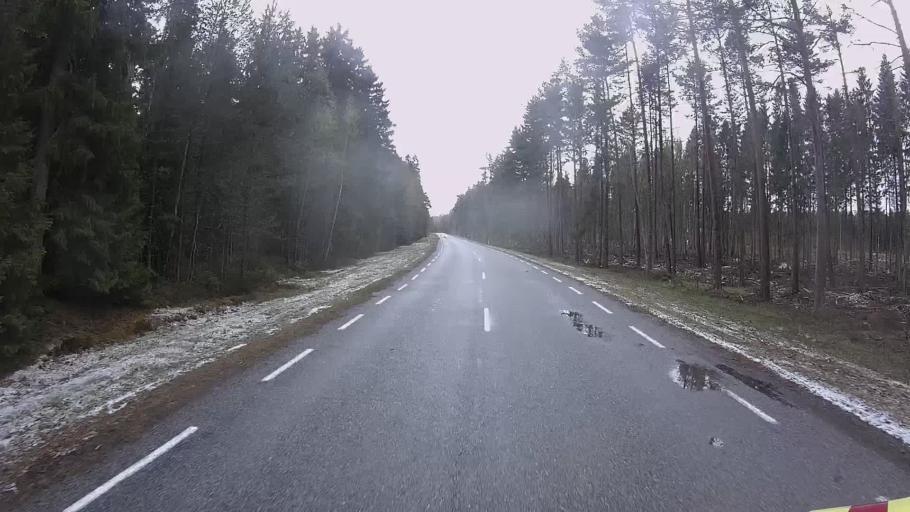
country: EE
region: Hiiumaa
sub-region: Kaerdla linn
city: Kardla
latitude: 59.0472
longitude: 22.6813
